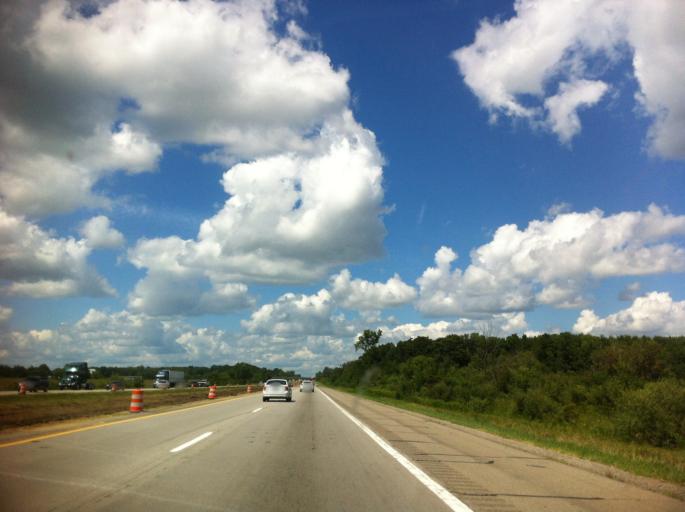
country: US
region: Michigan
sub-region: Washtenaw County
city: Milan
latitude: 42.1248
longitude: -83.6827
